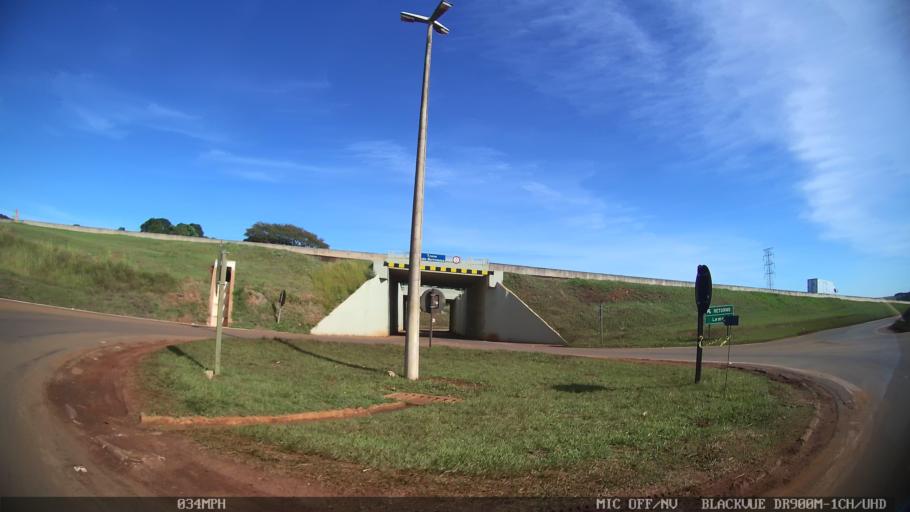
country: BR
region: Sao Paulo
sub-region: Araras
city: Araras
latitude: -22.3127
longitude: -47.3904
